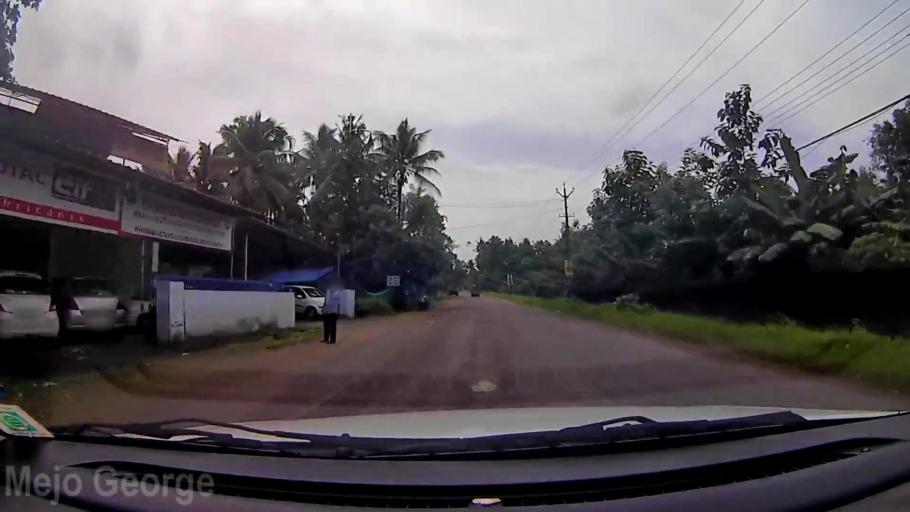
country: IN
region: Kerala
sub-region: Thrissur District
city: Kizhake Chalakudi
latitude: 10.3309
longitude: 76.3160
